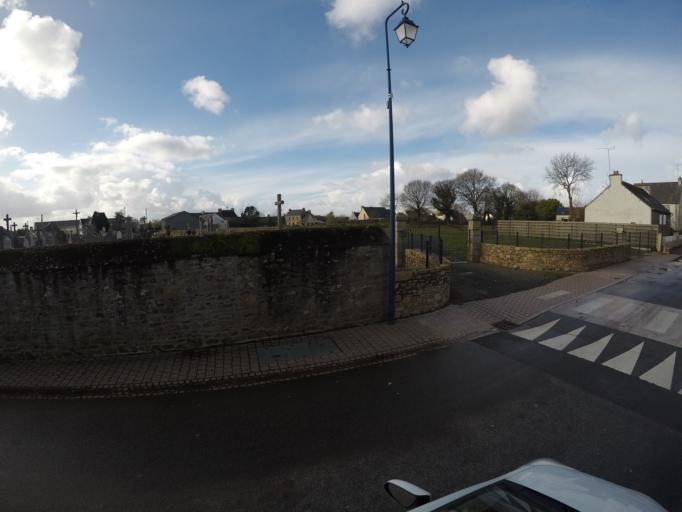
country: FR
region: Brittany
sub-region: Departement des Cotes-d'Armor
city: Lanvollon
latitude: 48.6341
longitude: -2.9870
